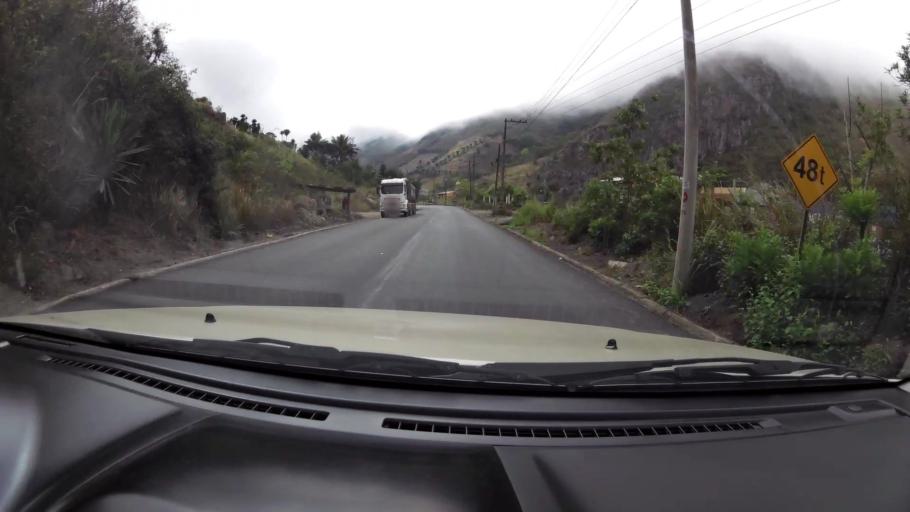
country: EC
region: El Oro
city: Pasaje
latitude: -3.3078
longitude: -79.5111
